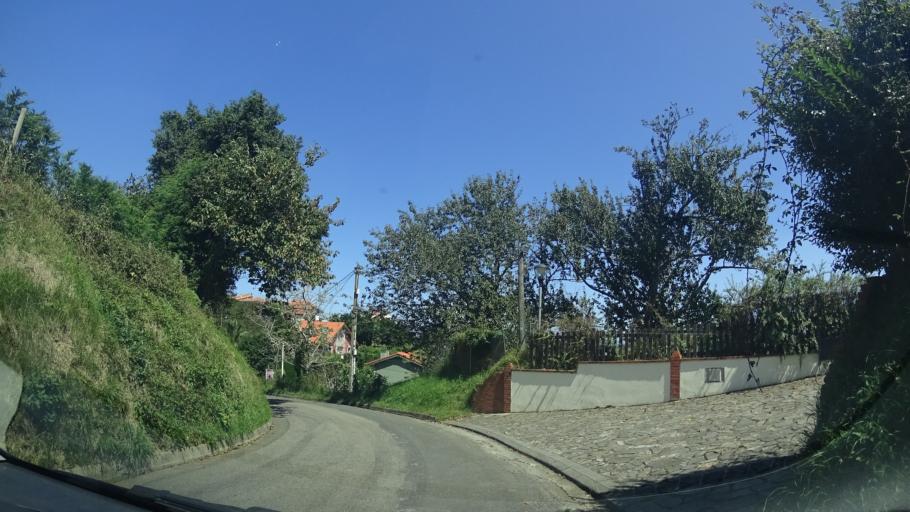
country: ES
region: Asturias
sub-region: Province of Asturias
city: Ribadesella
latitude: 43.4484
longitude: -5.0768
